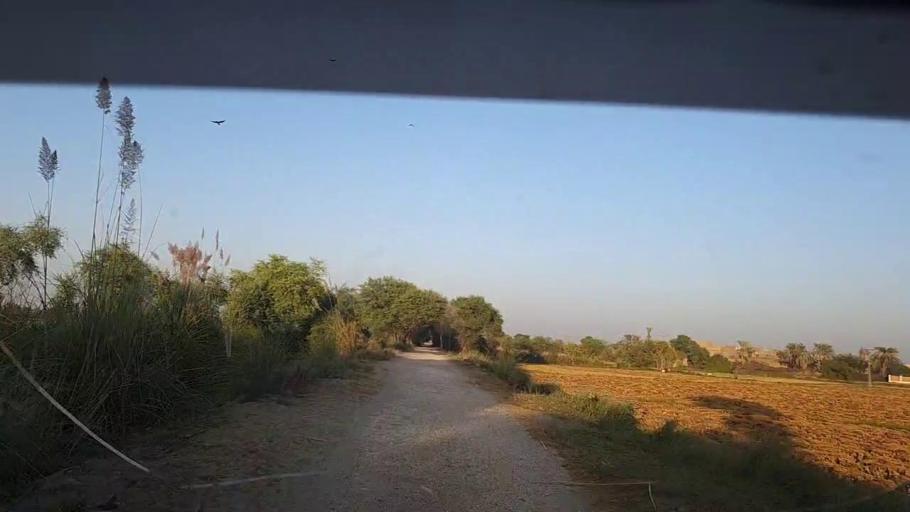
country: PK
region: Sindh
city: Ratodero
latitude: 27.8764
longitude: 68.2002
